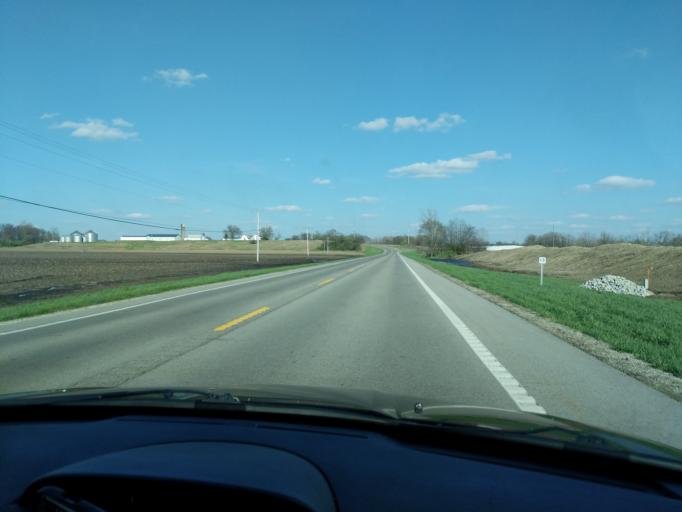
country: US
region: Ohio
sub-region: Champaign County
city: Urbana
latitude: 40.1069
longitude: -83.7892
